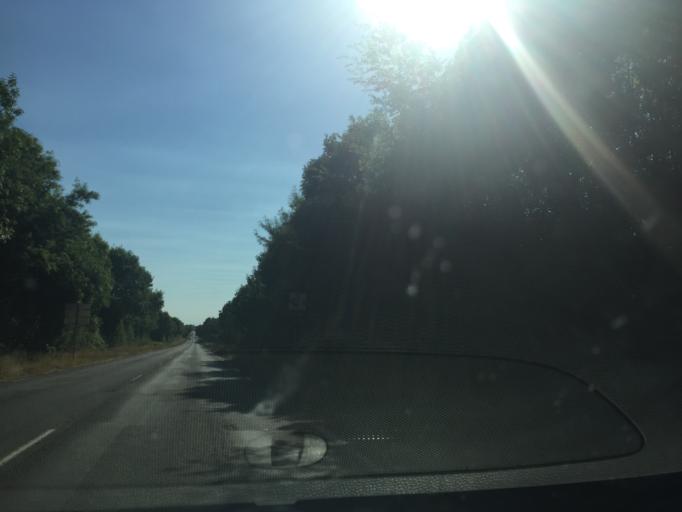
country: FR
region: Poitou-Charentes
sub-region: Departement des Deux-Sevres
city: Melle
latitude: 46.2345
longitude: -0.1145
